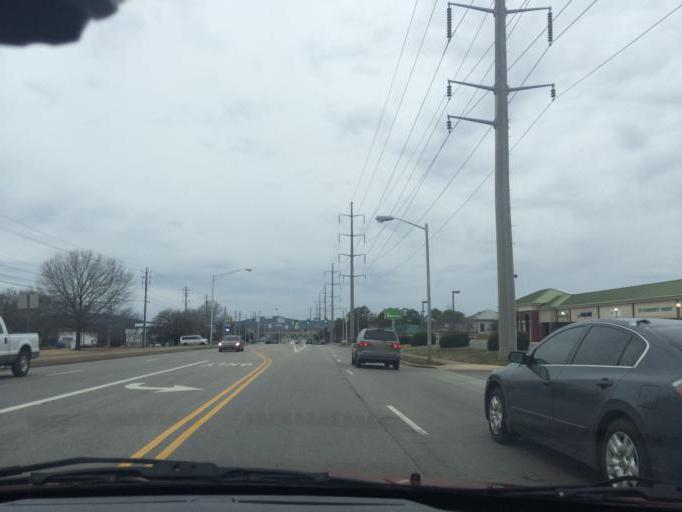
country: US
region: Alabama
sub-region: Madison County
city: Huntsville
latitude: 34.6912
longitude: -86.5725
